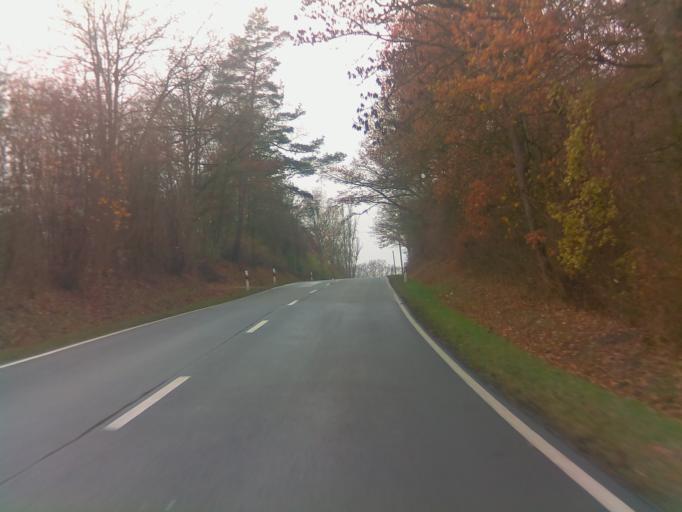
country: DE
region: Thuringia
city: Juchsen
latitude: 50.4286
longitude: 10.4795
